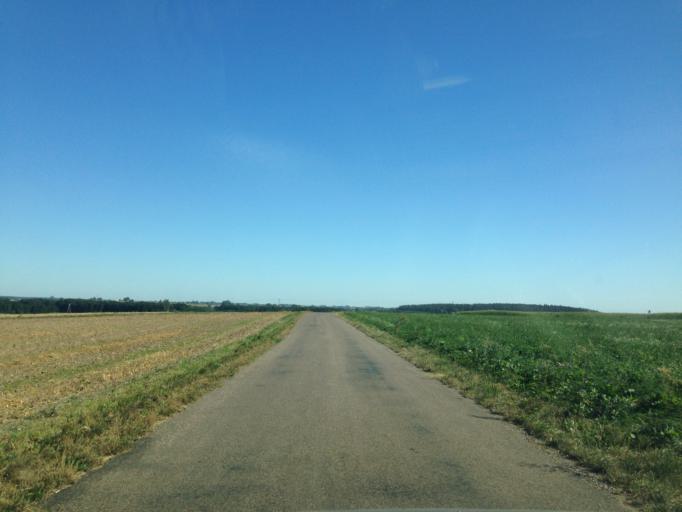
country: PL
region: Kujawsko-Pomorskie
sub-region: Powiat brodnicki
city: Swiedziebnia
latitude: 53.2034
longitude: 19.5261
